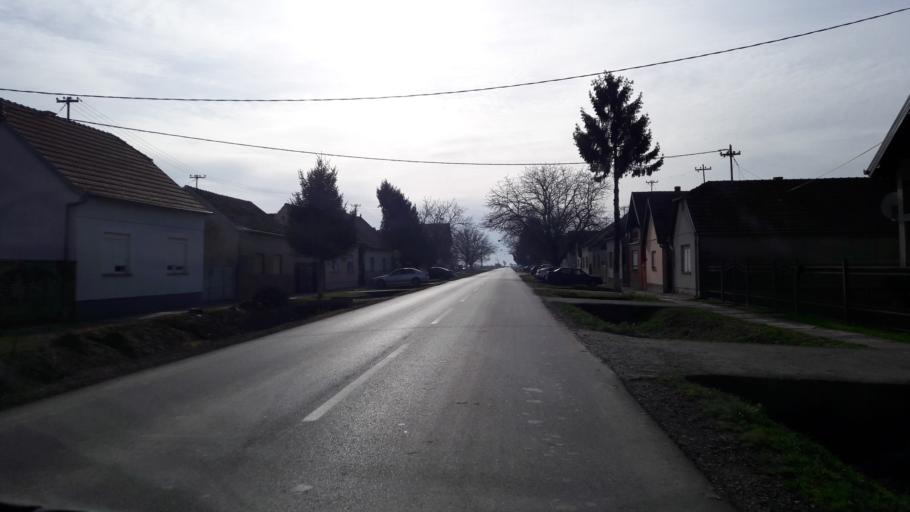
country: HR
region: Osjecko-Baranjska
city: Semeljci
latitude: 45.3464
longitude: 18.5575
